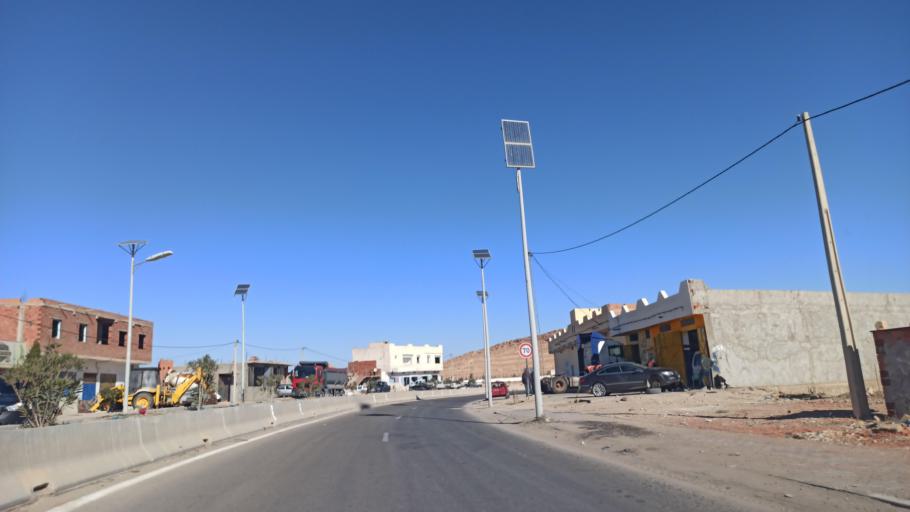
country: TN
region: Gafsa
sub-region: Gafsa Municipality
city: Gafsa
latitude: 34.4498
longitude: 8.7730
